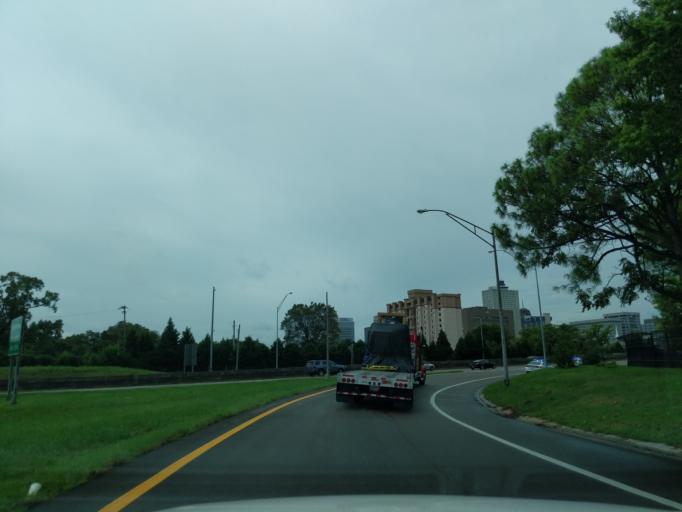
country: US
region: Tennessee
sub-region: Shelby County
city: Memphis
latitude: 35.1523
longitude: -90.0421
